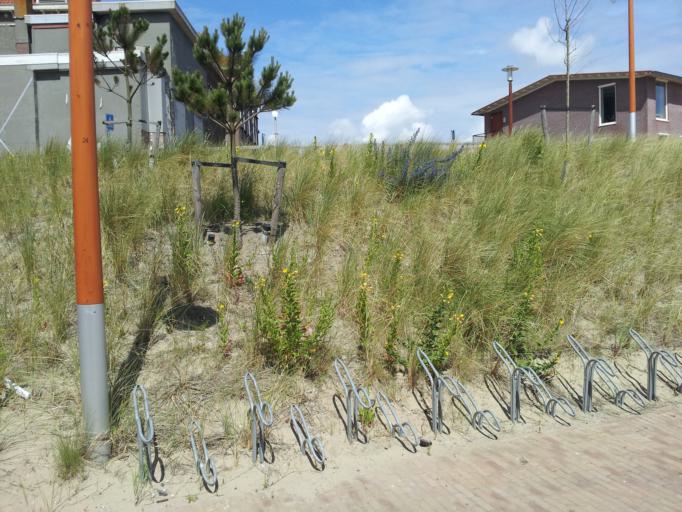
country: NL
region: South Holland
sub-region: Gemeente Katwijk
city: Katwijk aan Zee
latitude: 52.1972
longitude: 4.3911
